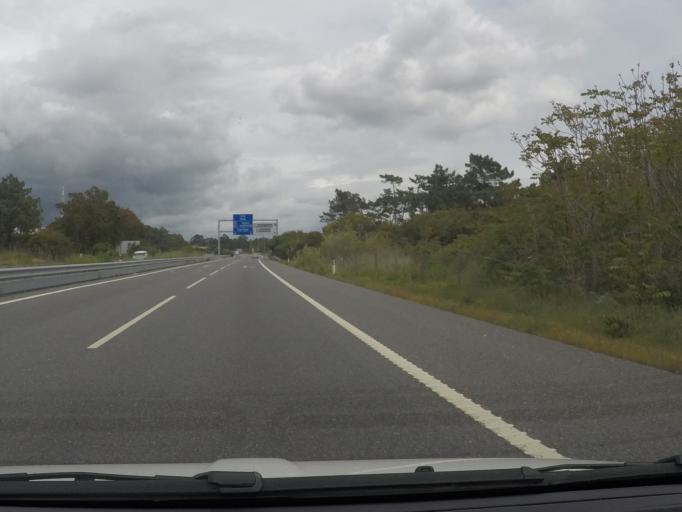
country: PT
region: Setubal
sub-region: Sines
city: Sines
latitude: 37.9735
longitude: -8.8155
